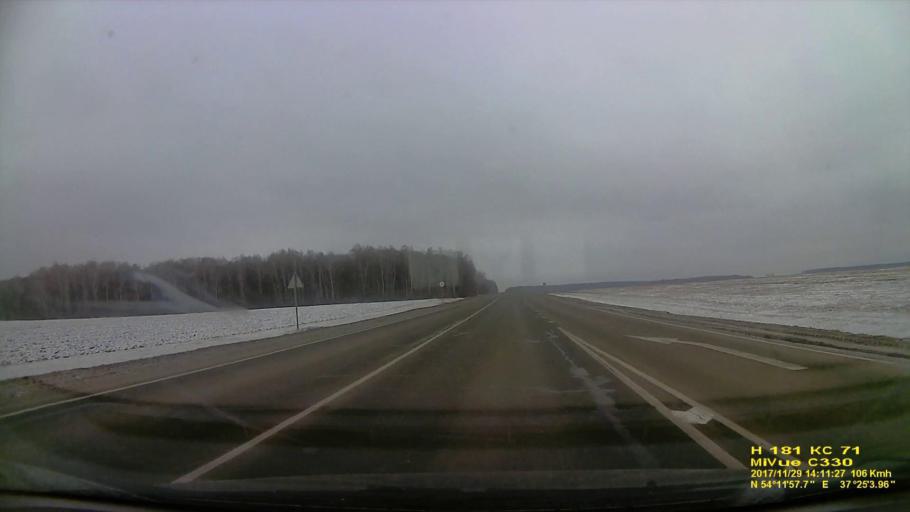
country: RU
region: Tula
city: Barsuki
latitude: 54.1991
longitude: 37.4182
